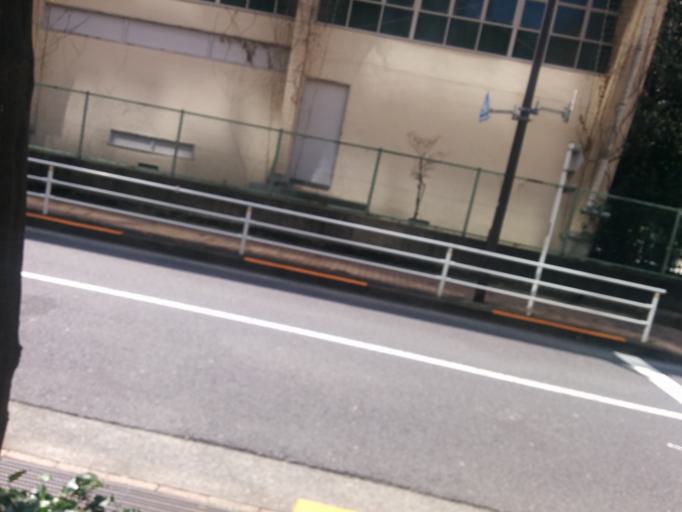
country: JP
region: Tokyo
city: Tokyo
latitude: 35.6943
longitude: 139.6883
